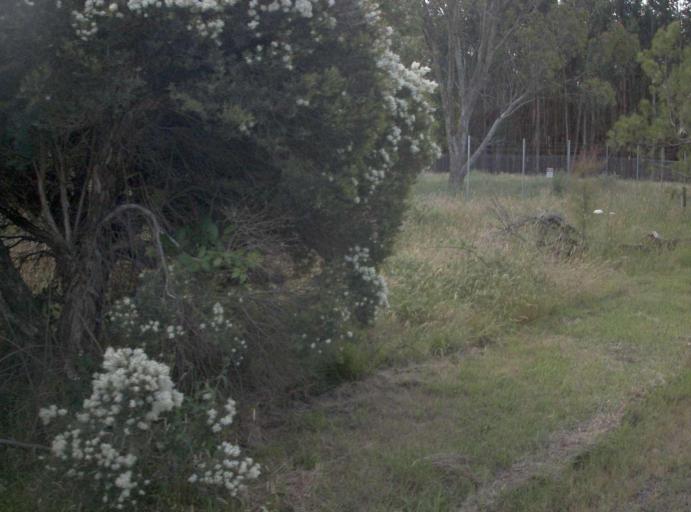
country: AU
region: Victoria
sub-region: Latrobe
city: Morwell
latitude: -38.1966
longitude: 146.4026
